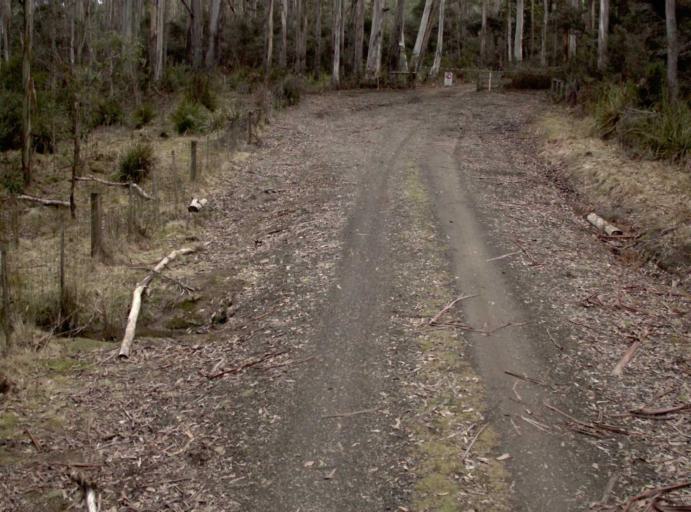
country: AU
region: Tasmania
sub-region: Launceston
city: Newstead
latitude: -41.3059
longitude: 147.3117
